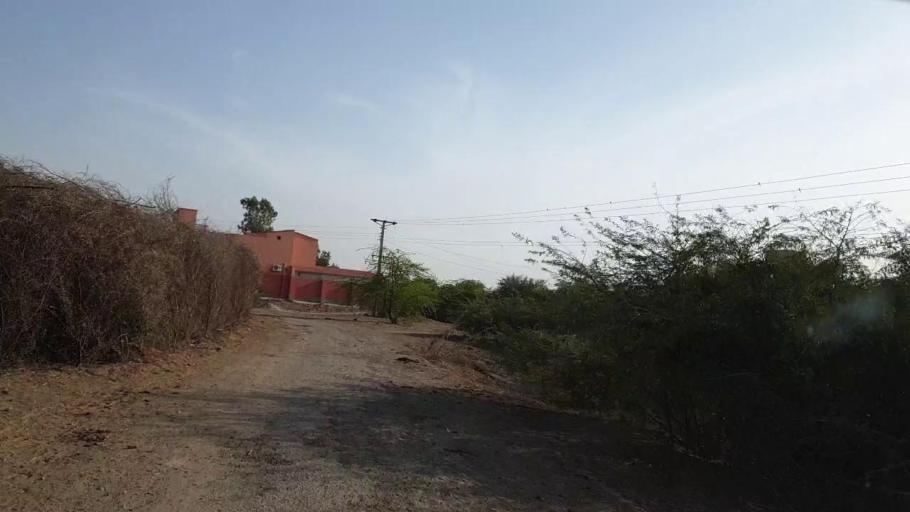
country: PK
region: Sindh
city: Kunri
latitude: 25.0745
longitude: 69.4357
